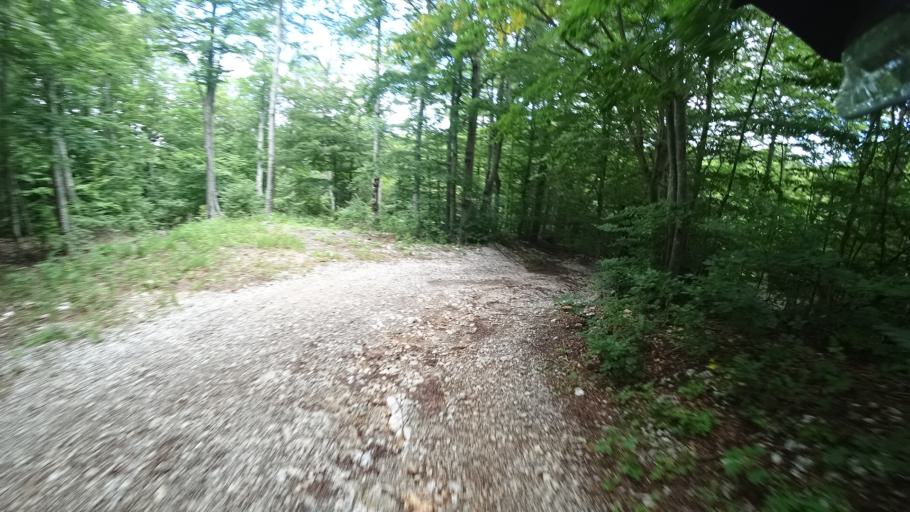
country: HR
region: Primorsko-Goranska
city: Bribir
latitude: 45.2378
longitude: 14.7743
